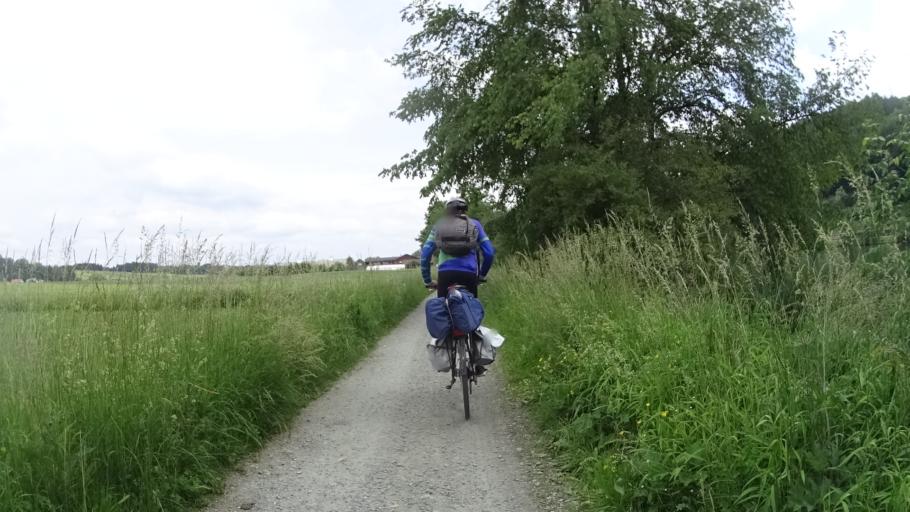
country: DE
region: Bavaria
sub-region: Lower Bavaria
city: Aicha vorm Wald
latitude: 48.6046
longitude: 13.3189
